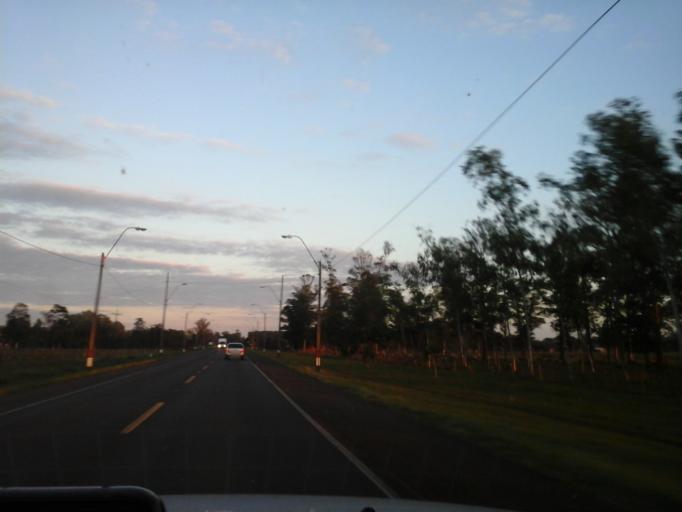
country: PY
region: Itapua
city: General Delgado
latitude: -27.0868
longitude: -56.5355
